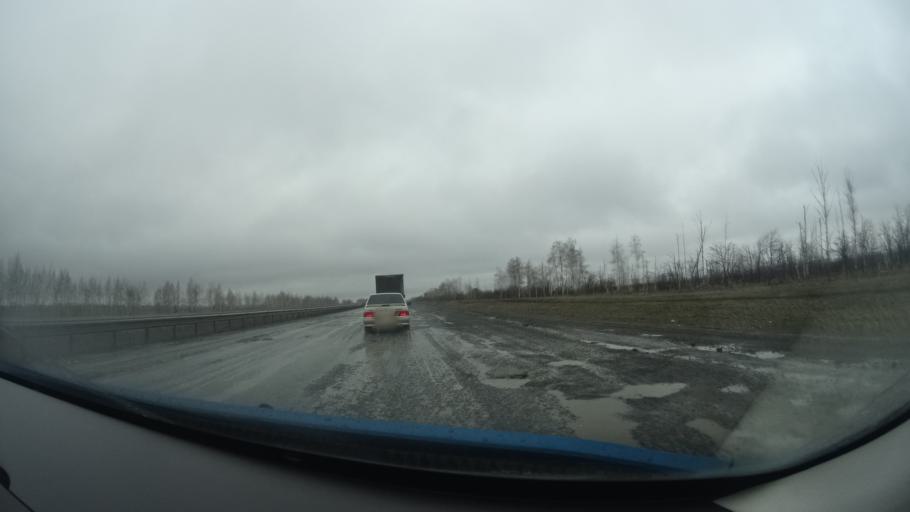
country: RU
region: Bashkortostan
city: Buzdyak
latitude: 54.6534
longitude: 54.6275
